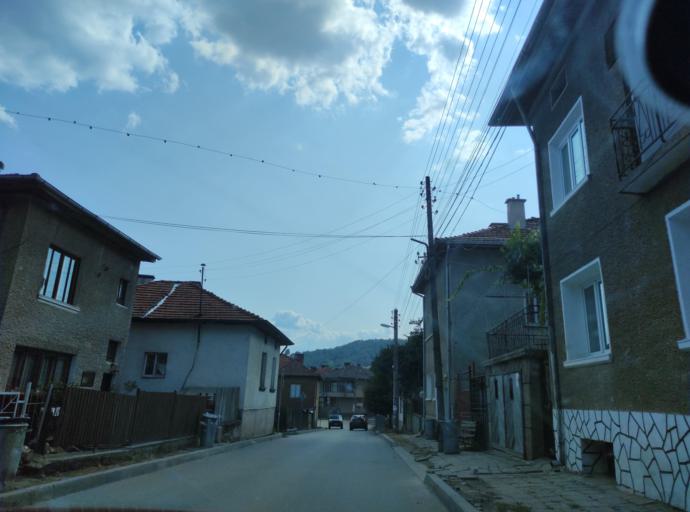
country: BG
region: Blagoevgrad
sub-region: Obshtina Belitsa
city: Belitsa
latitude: 41.9516
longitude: 23.5560
